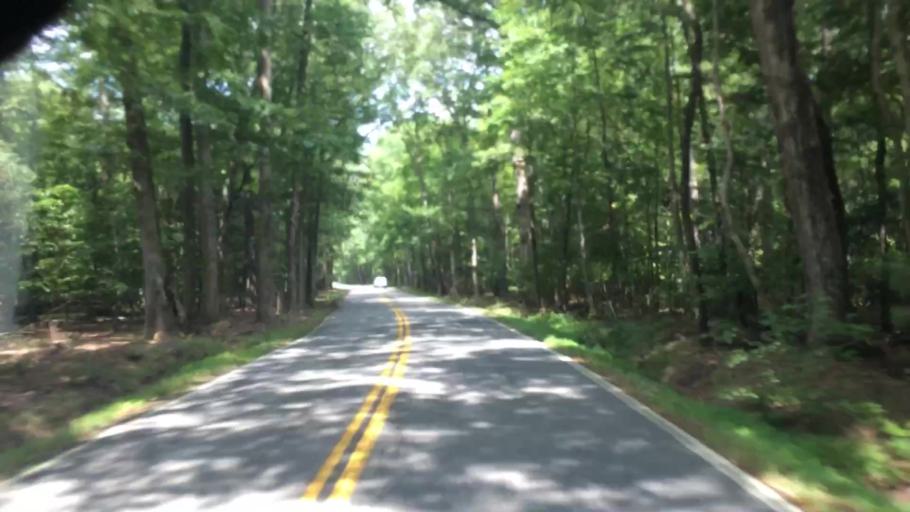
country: US
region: Virginia
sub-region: James City County
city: Williamsburg
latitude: 37.2397
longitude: -76.7888
